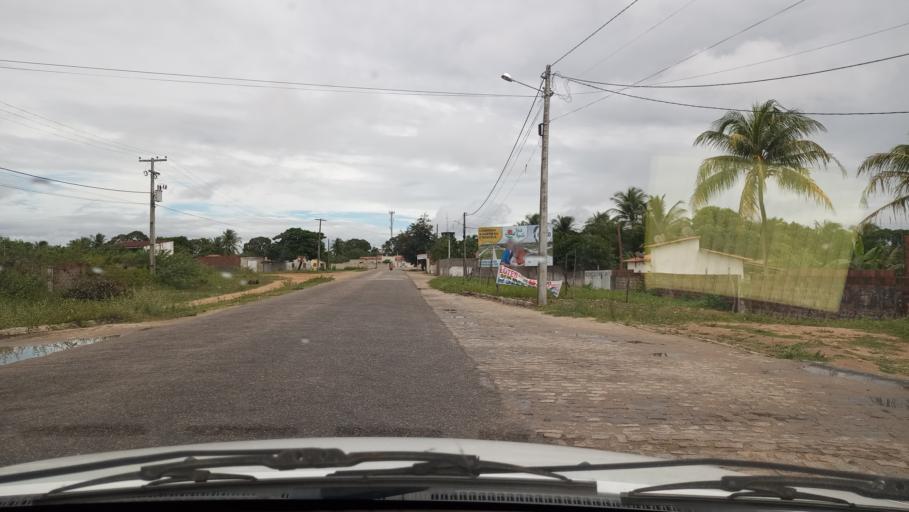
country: BR
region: Rio Grande do Norte
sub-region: Poco Branco
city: Poco Branco
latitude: -5.6175
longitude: -35.6534
